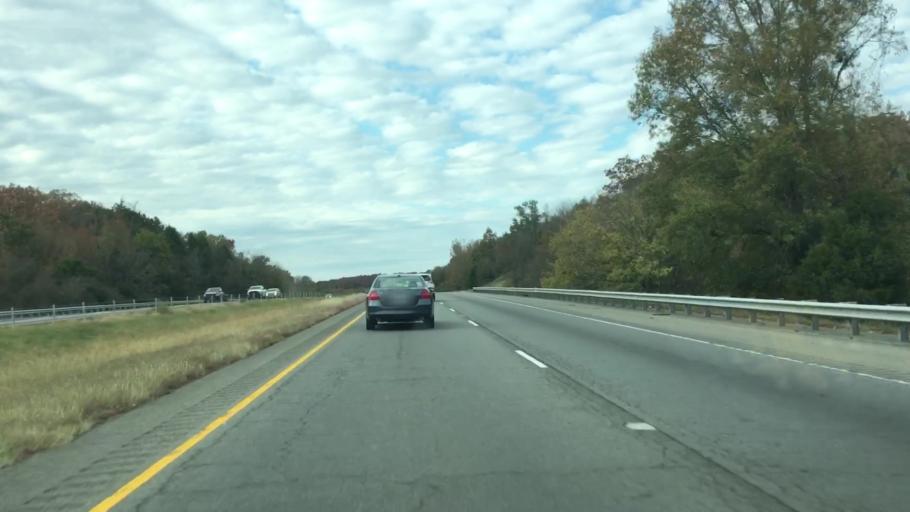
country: US
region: Arkansas
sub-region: Faulkner County
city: Conway
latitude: 35.1338
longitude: -92.5178
